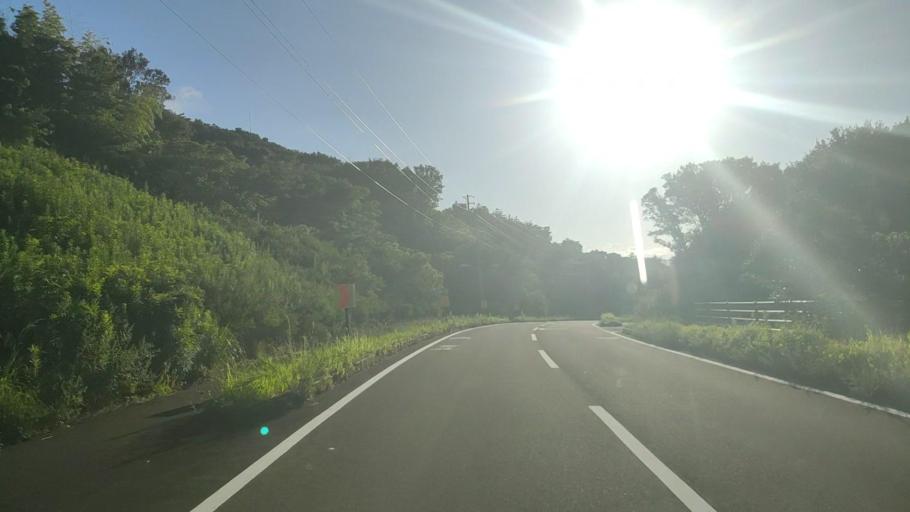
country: JP
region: Mie
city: Toba
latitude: 34.2737
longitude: 136.7761
